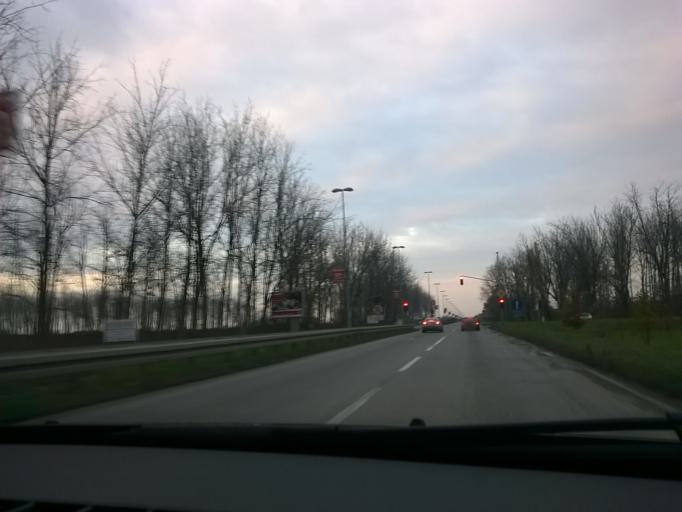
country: RS
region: Autonomna Pokrajina Vojvodina
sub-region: Juznobacki Okrug
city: Novi Sad
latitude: 45.2795
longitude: 19.8507
